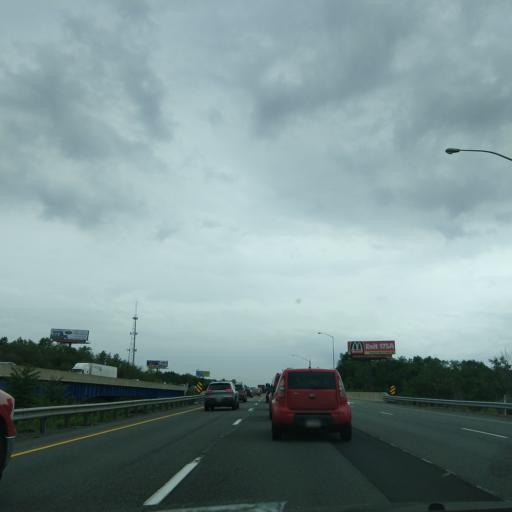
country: US
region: Pennsylvania
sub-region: Lackawanna County
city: Moosic
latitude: 41.3509
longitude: -75.7258
